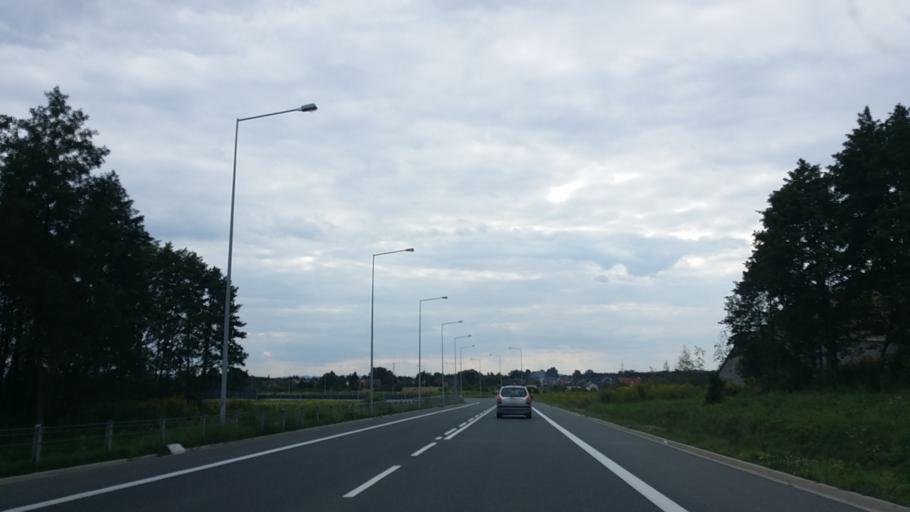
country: PL
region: Lesser Poland Voivodeship
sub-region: Powiat krakowski
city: Skawina
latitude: 49.9885
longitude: 19.8273
